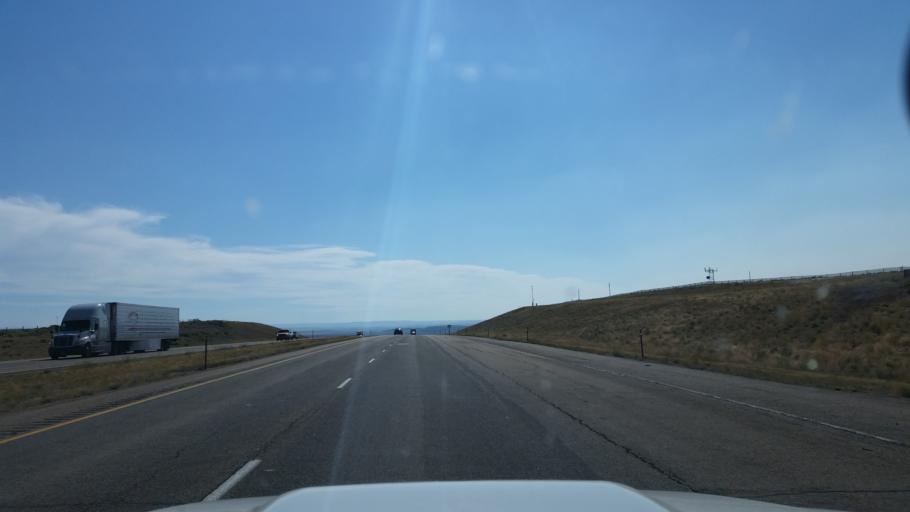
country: US
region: Wyoming
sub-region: Uinta County
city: Lyman
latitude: 41.4310
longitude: -110.1151
